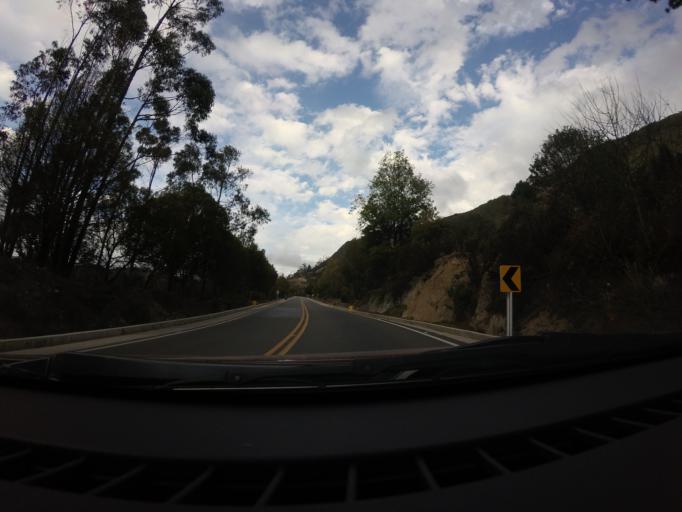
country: CO
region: Boyaca
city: Cucaita
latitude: 5.5495
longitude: -73.4366
